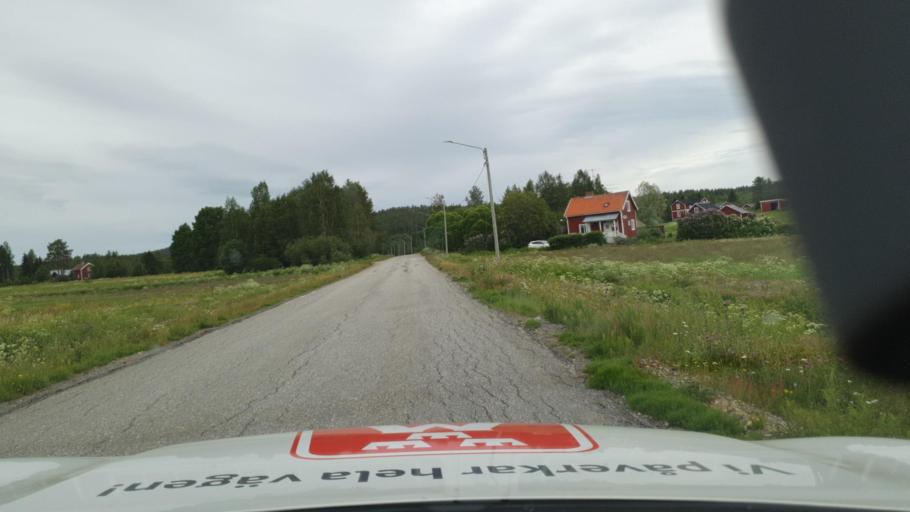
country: SE
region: Vaesterbotten
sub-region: Skelleftea Kommun
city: Burtraesk
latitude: 64.3058
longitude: 20.6518
